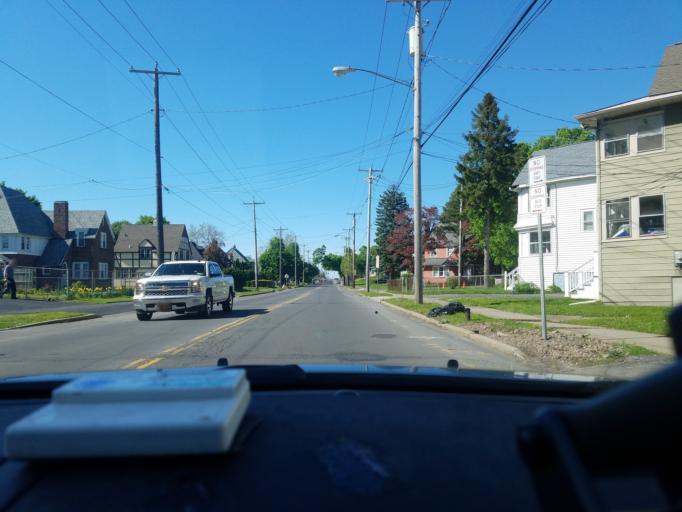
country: US
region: New York
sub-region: Onondaga County
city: Lyncourt
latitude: 43.0695
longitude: -76.1230
